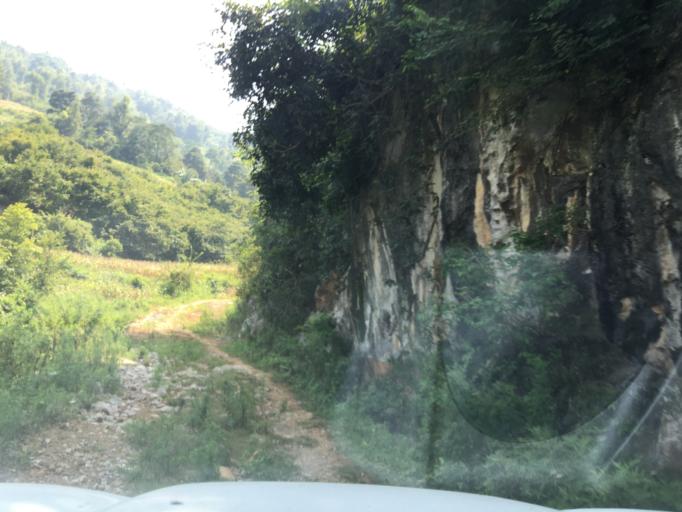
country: CN
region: Guangxi Zhuangzu Zizhiqu
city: Xinzhou
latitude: 24.9927
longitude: 105.7431
